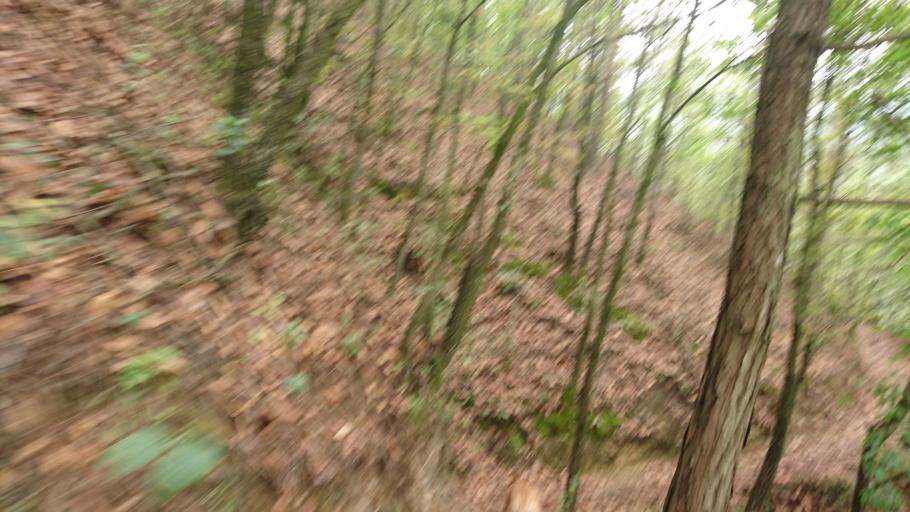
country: MX
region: Nuevo Leon
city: Garza Garcia
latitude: 25.6012
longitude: -100.3350
